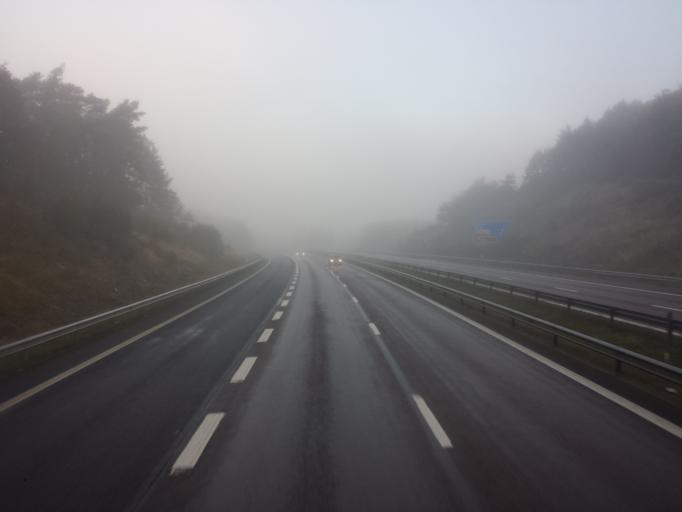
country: SE
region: Halland
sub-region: Kungsbacka Kommun
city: Fjaeras kyrkby
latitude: 57.4289
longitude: 12.1593
